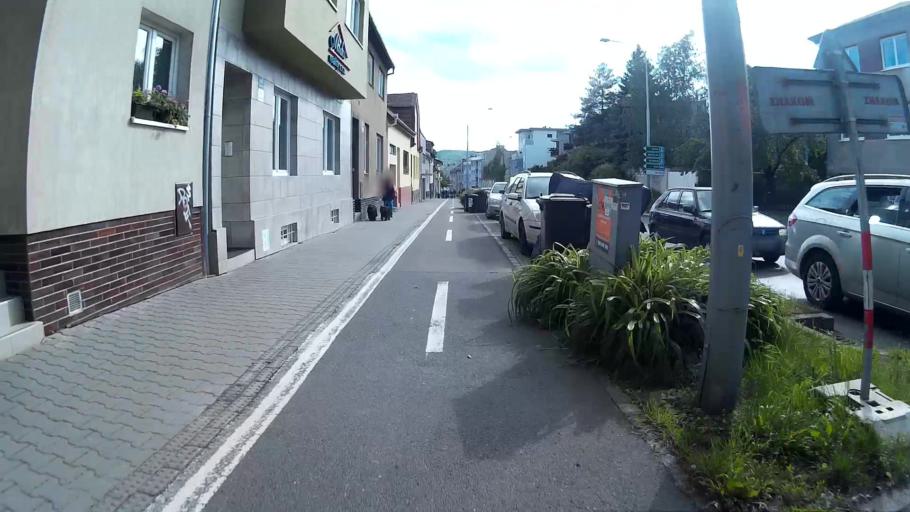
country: CZ
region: South Moravian
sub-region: Mesto Brno
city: Brno
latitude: 49.2178
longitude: 16.5729
